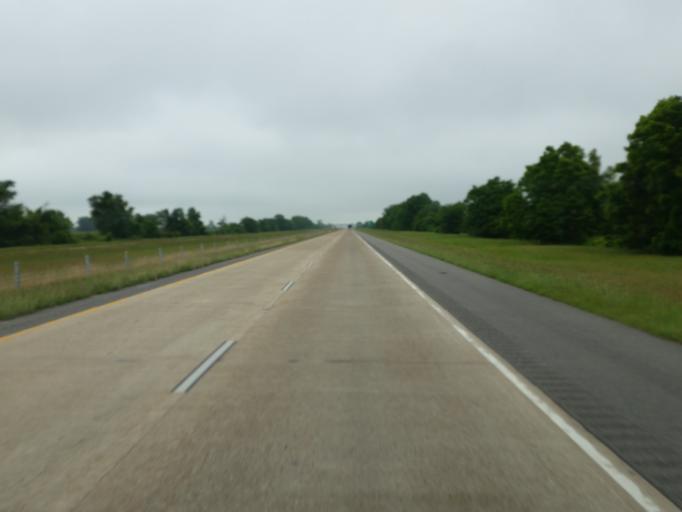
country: US
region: Mississippi
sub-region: Warren County
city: Vicksburg
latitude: 32.3320
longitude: -91.0380
